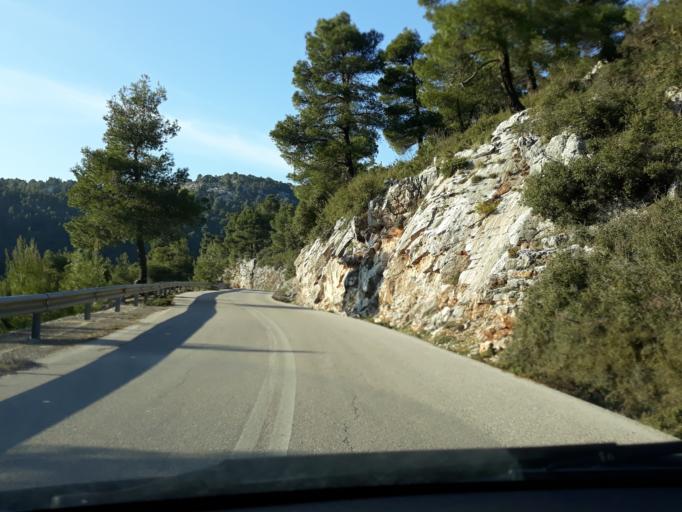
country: GR
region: Attica
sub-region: Nomarchia Dytikis Attikis
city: Fyli
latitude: 38.1510
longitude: 23.6317
